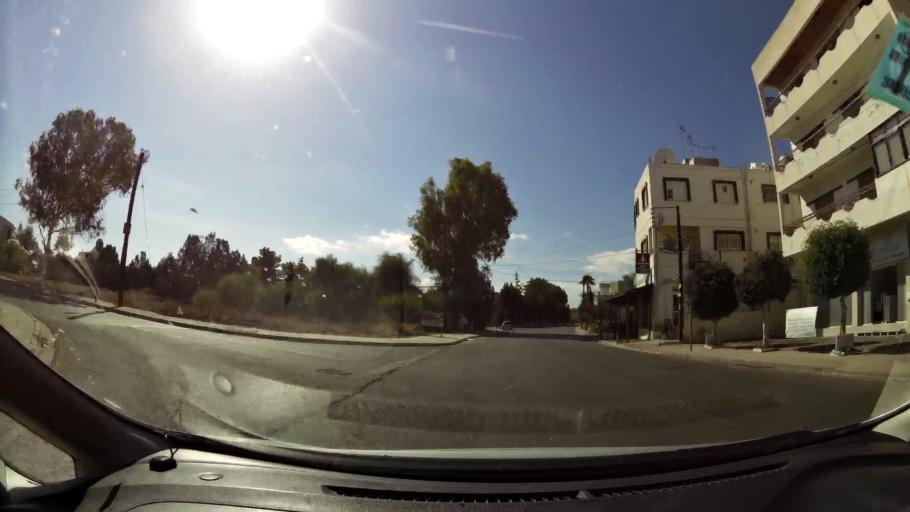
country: CY
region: Lefkosia
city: Nicosia
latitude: 35.1383
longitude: 33.3365
